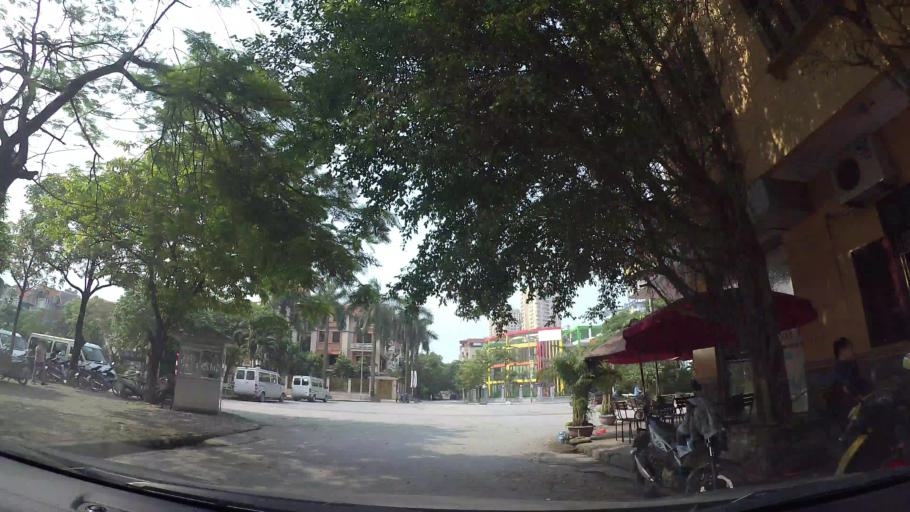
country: VN
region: Ha Noi
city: Van Dien
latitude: 20.9751
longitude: 105.8345
